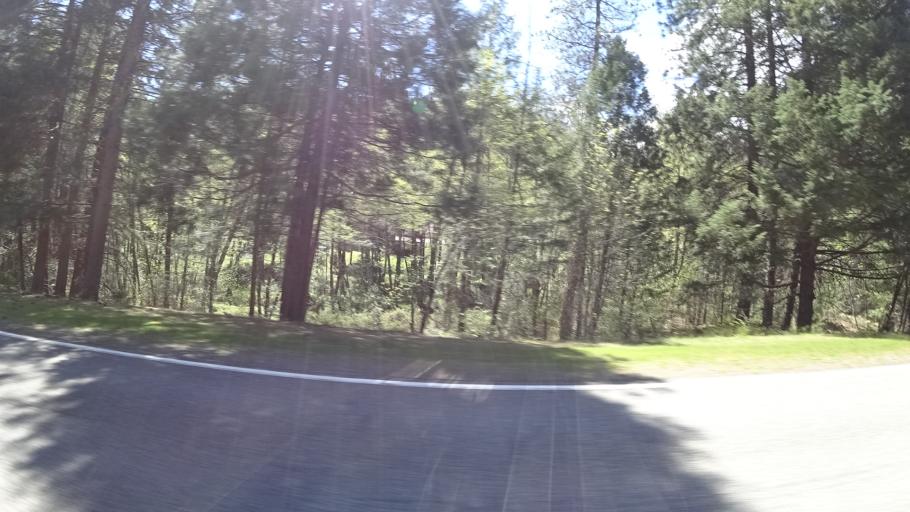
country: US
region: California
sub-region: Trinity County
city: Weaverville
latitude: 40.7765
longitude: -122.8929
